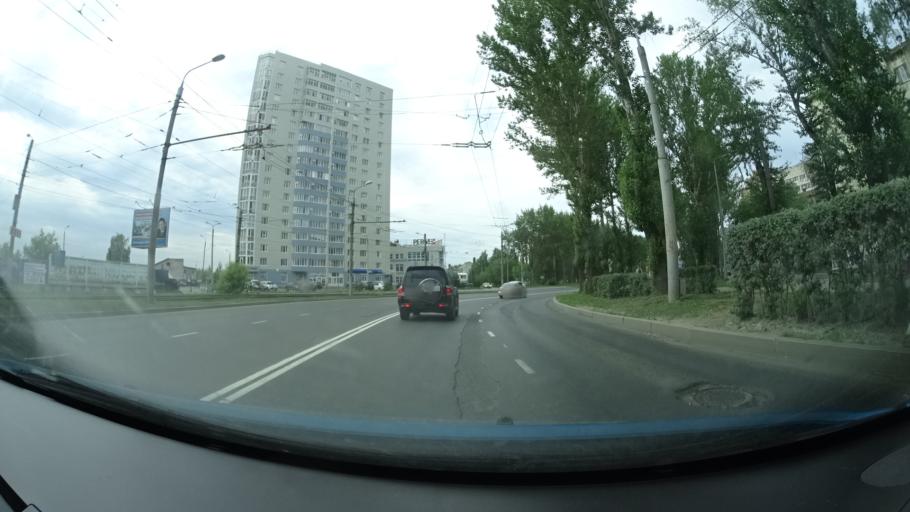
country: RU
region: Perm
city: Perm
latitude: 58.0112
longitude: 56.2803
